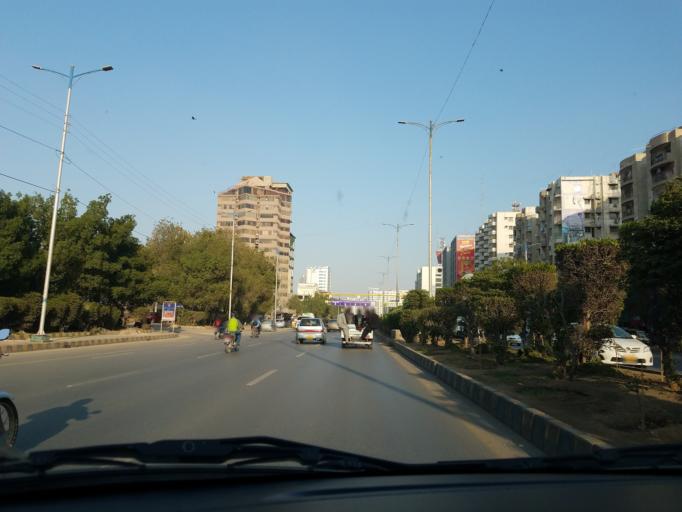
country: PK
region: Sindh
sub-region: Karachi District
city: Karachi
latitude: 24.8617
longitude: 67.0680
